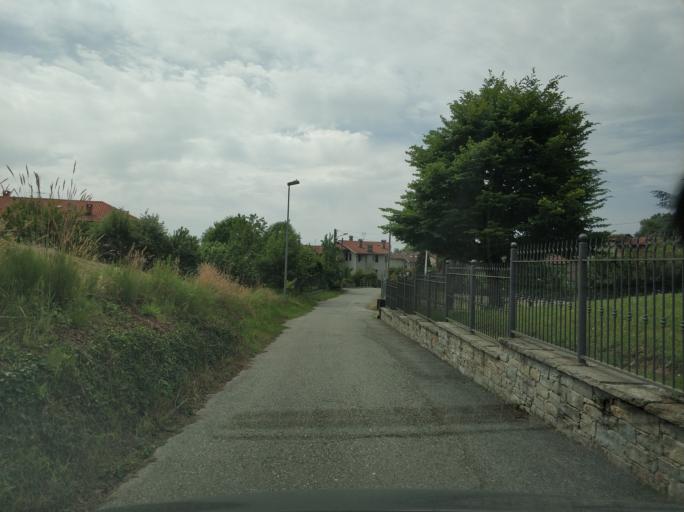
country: IT
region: Piedmont
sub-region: Provincia di Torino
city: Levone
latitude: 45.3216
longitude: 7.6056
